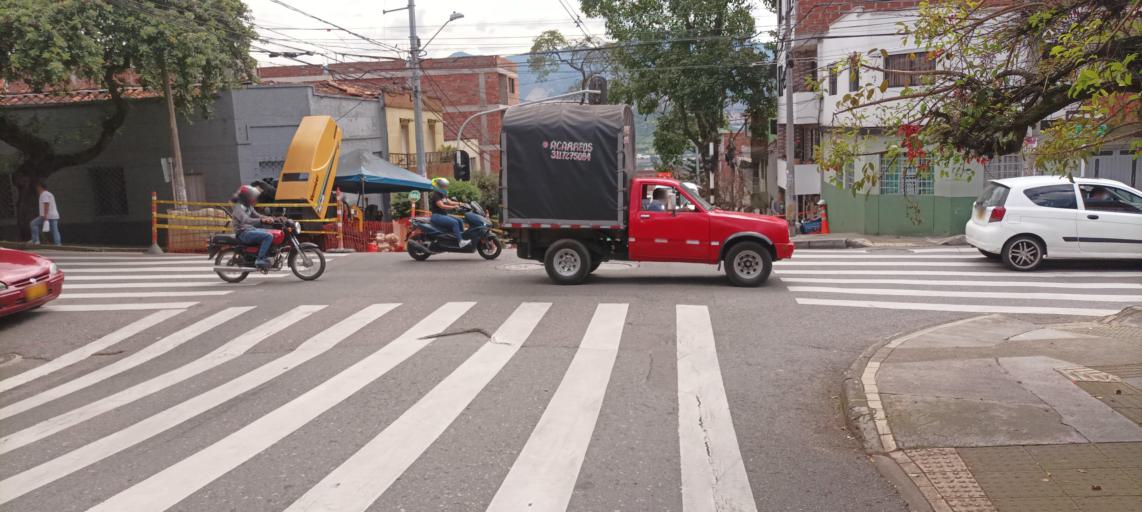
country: CO
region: Antioquia
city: Medellin
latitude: 6.2663
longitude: -75.5538
